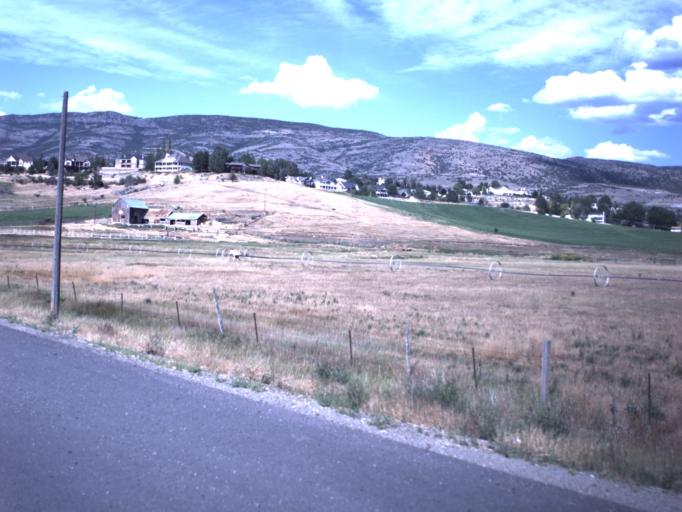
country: US
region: Utah
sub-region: Wasatch County
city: Heber
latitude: 40.5189
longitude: -111.4116
